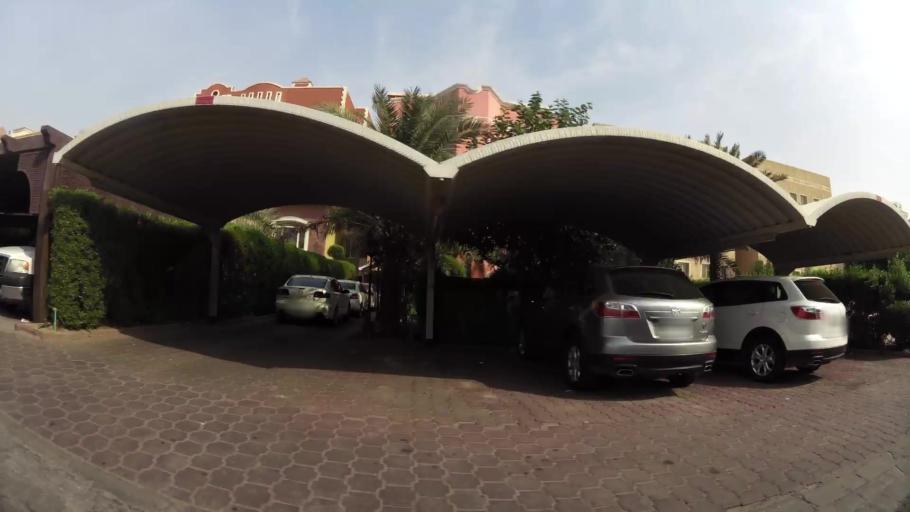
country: KW
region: Al Asimah
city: Ar Rabiyah
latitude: 29.2786
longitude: 47.9272
